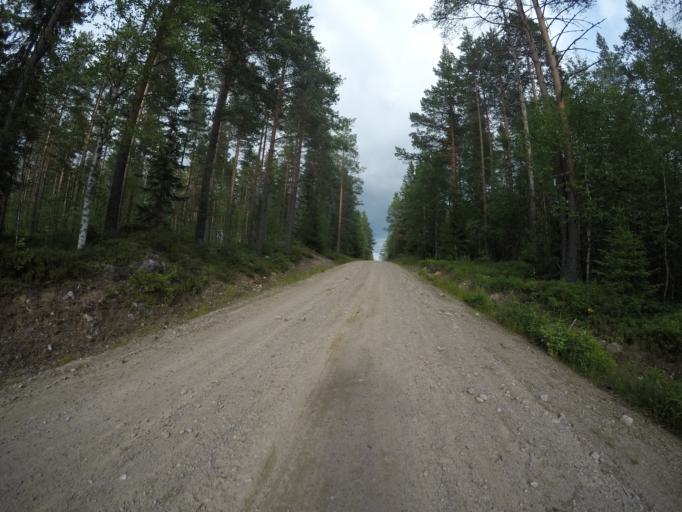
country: SE
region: Vaermland
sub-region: Filipstads Kommun
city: Lesjofors
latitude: 60.1984
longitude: 14.3503
